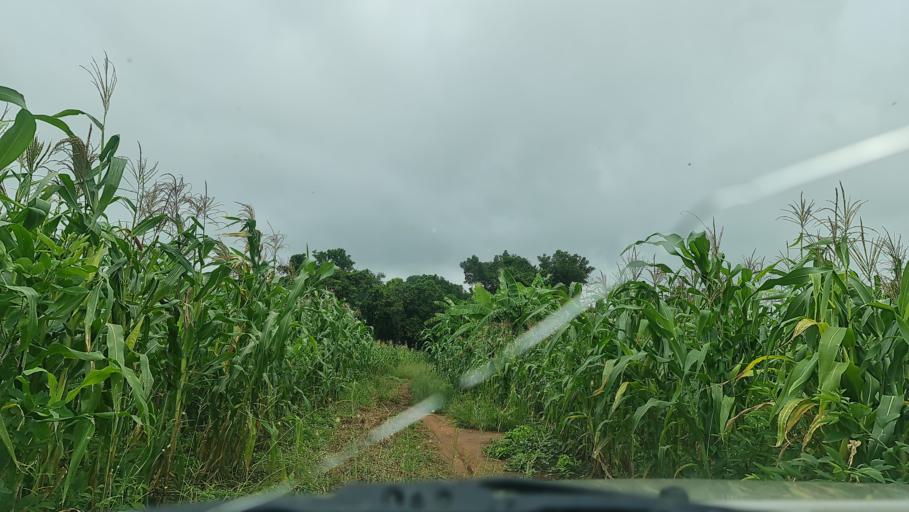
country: MW
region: Southern Region
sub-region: Nsanje District
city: Nsanje
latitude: -17.3855
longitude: 35.7787
